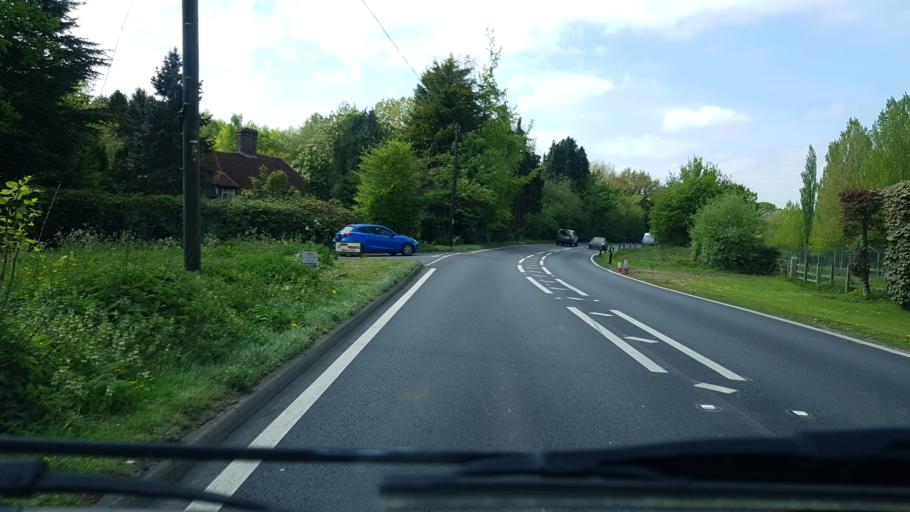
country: GB
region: England
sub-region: East Sussex
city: Wadhurst
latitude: 51.0723
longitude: 0.4250
